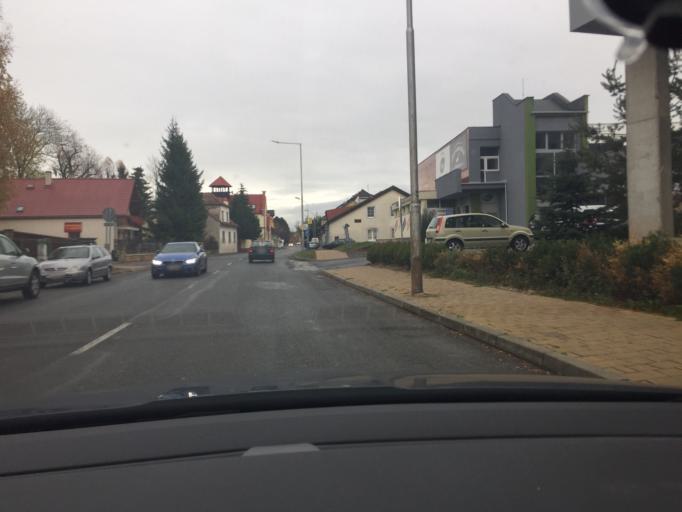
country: SK
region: Presovsky
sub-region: Okres Poprad
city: Poprad
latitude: 49.0669
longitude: 20.2807
